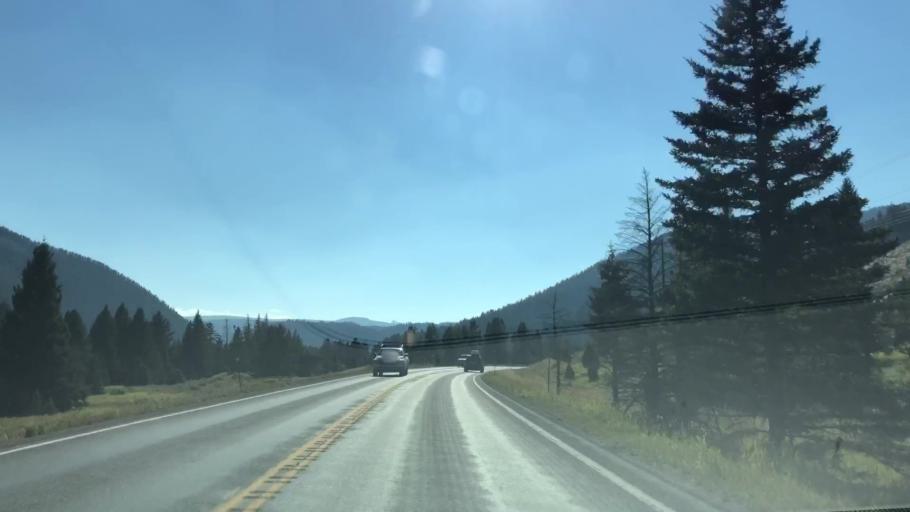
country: US
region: Montana
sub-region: Gallatin County
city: Big Sky
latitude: 45.2783
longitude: -111.2310
